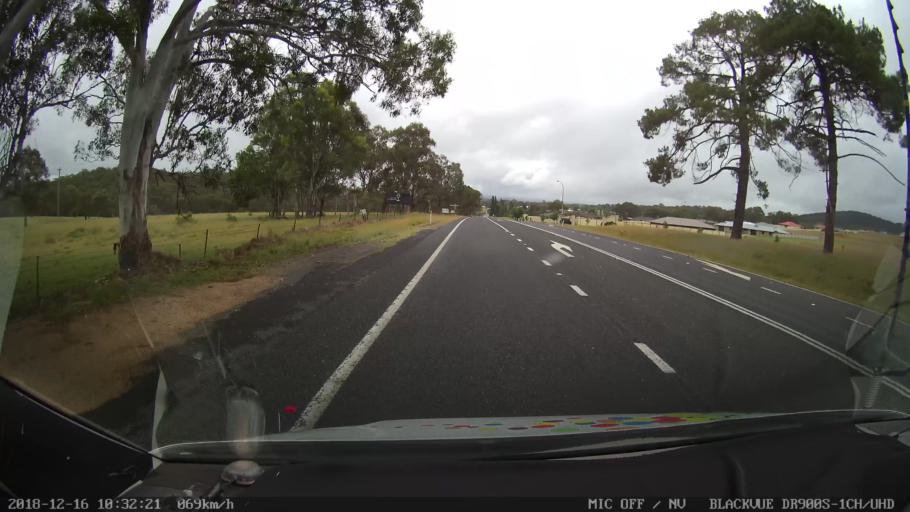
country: AU
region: New South Wales
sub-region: Tenterfield Municipality
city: Carrolls Creek
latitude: -29.0734
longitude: 152.0110
